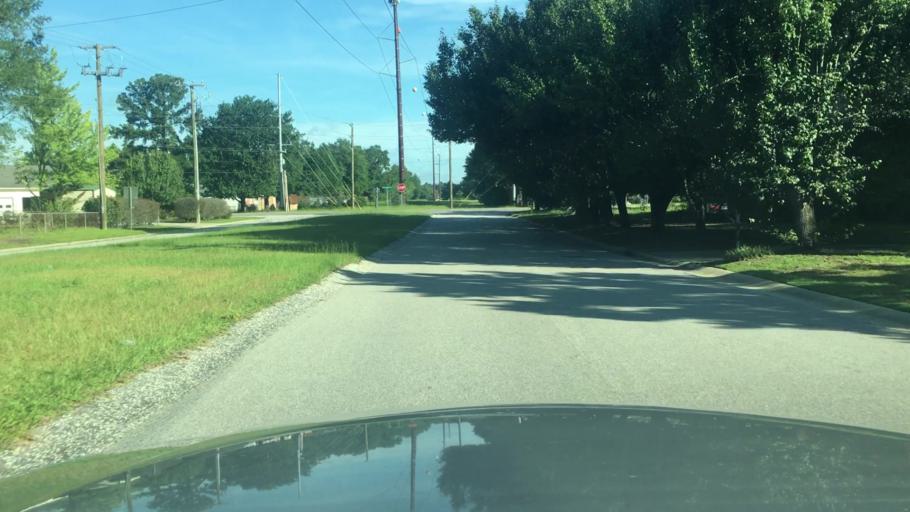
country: US
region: North Carolina
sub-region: Cumberland County
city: Fayetteville
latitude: 35.1322
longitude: -78.8930
